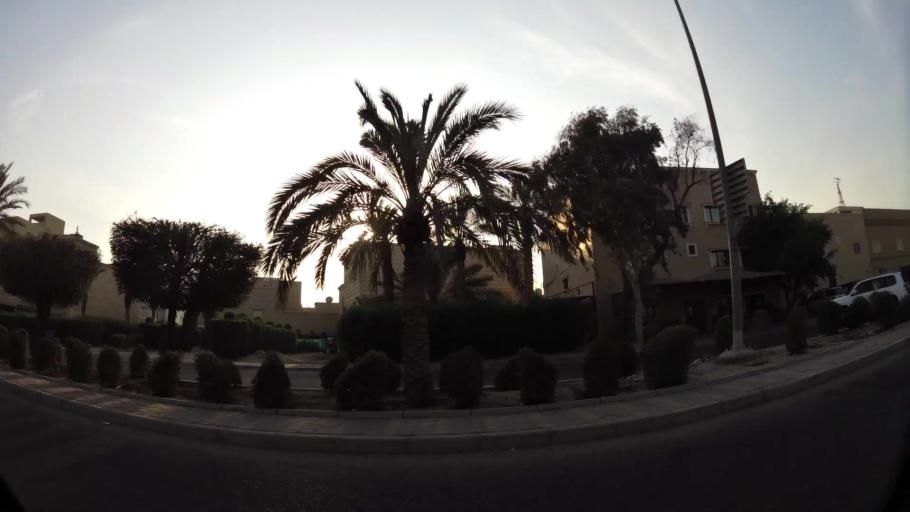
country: KW
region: Mubarak al Kabir
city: Sabah as Salim
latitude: 29.2565
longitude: 48.0701
